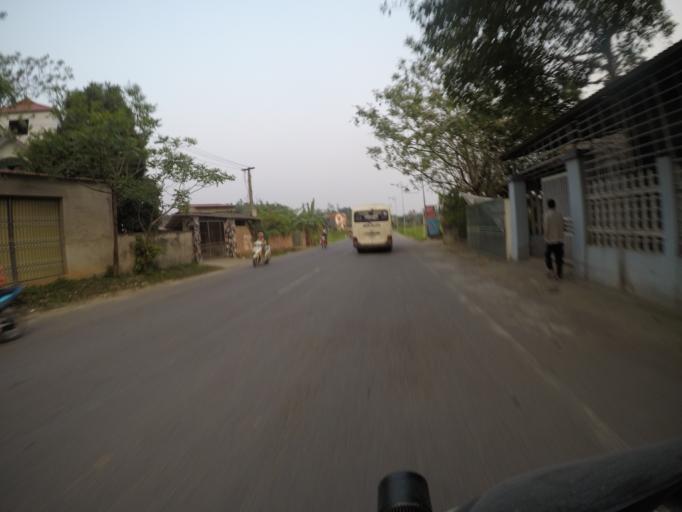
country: VN
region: Vinh Phuc
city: Trai Ngau
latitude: 21.4239
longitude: 105.5956
